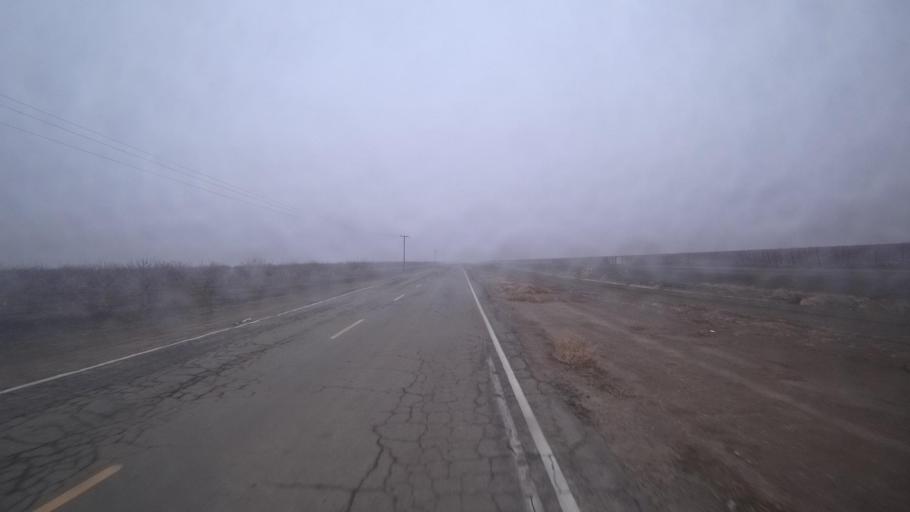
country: US
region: California
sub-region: Kern County
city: Lost Hills
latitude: 35.5175
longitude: -119.6171
